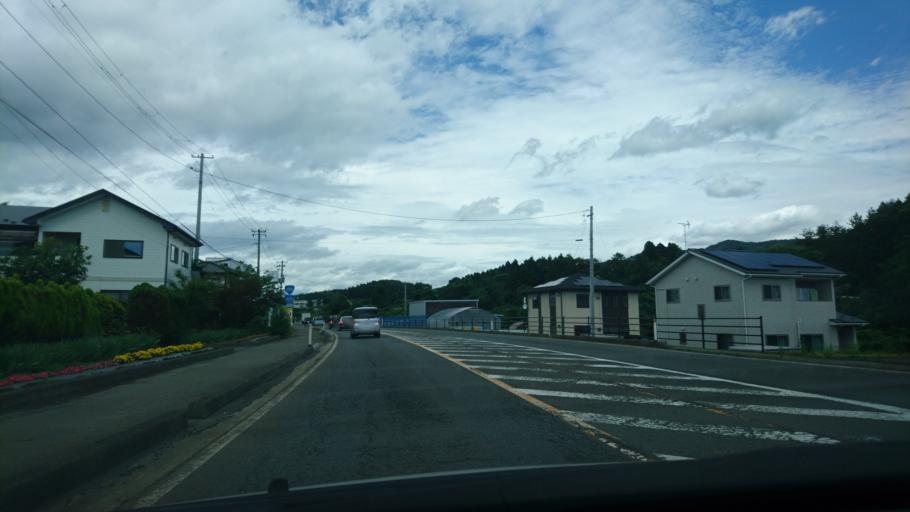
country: JP
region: Iwate
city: Morioka-shi
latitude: 39.6077
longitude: 141.2037
